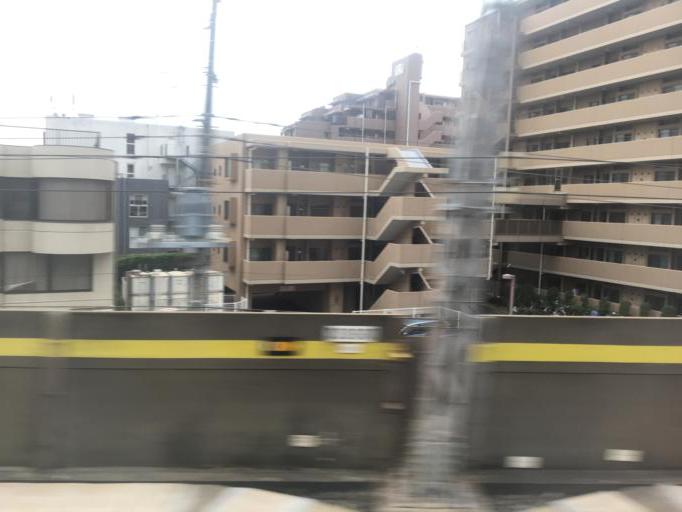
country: JP
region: Chiba
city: Funabashi
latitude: 35.7090
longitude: 139.9481
